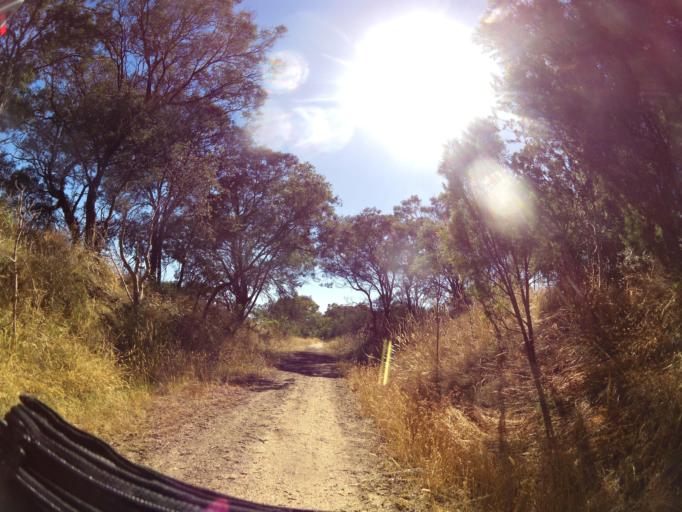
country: AU
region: Victoria
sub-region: Ballarat North
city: Delacombe
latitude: -37.6698
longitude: 143.4565
